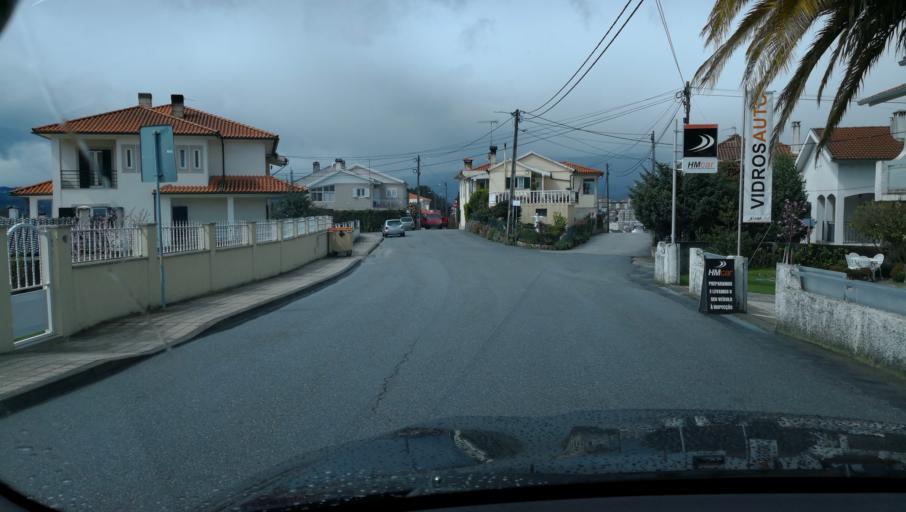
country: PT
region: Vila Real
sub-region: Vila Real
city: Vila Real
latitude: 41.3036
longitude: -7.7243
